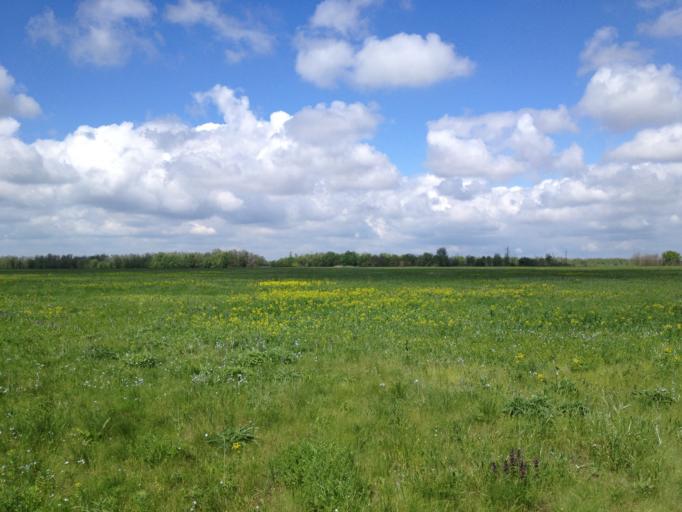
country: RU
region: Rostov
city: Rassvet
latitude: 46.8230
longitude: 40.8618
